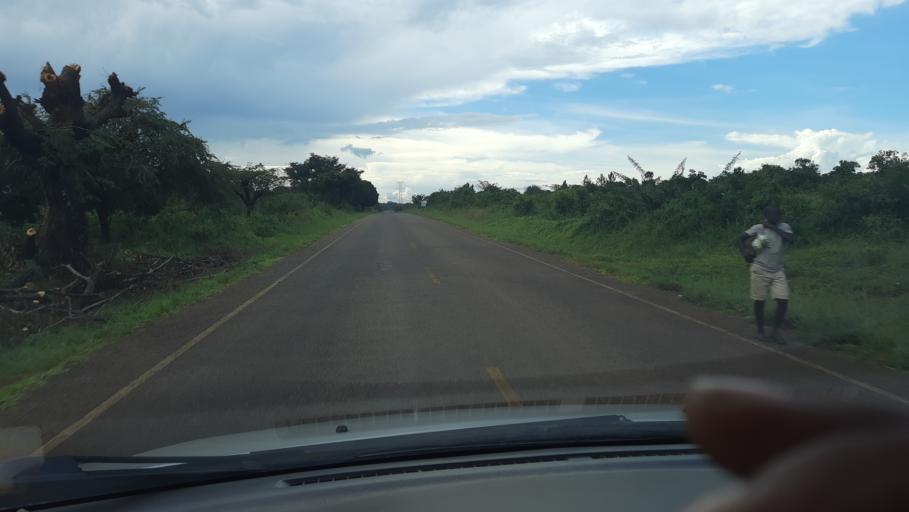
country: UG
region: Central Region
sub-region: Nakasongola District
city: Nakasongola
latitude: 1.3184
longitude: 32.4355
